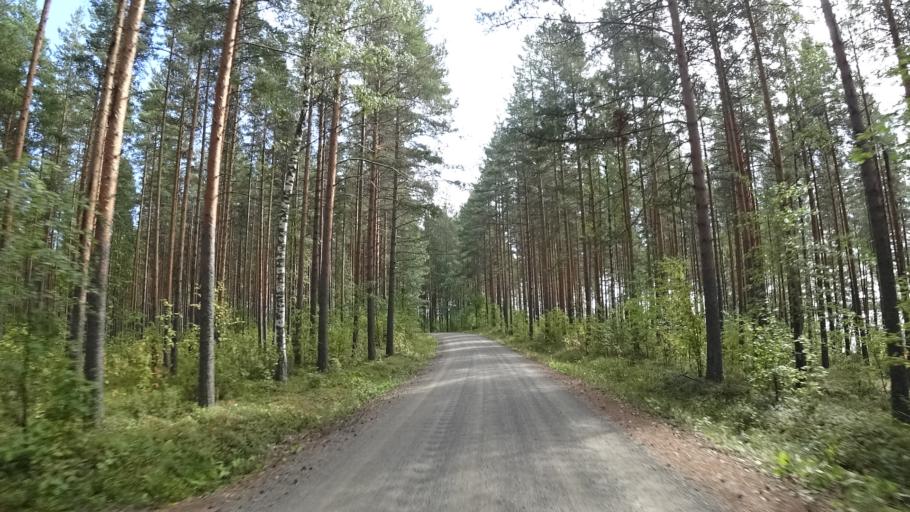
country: FI
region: North Karelia
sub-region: Keski-Karjala
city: Raeaekkylae
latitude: 62.3904
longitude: 29.7762
